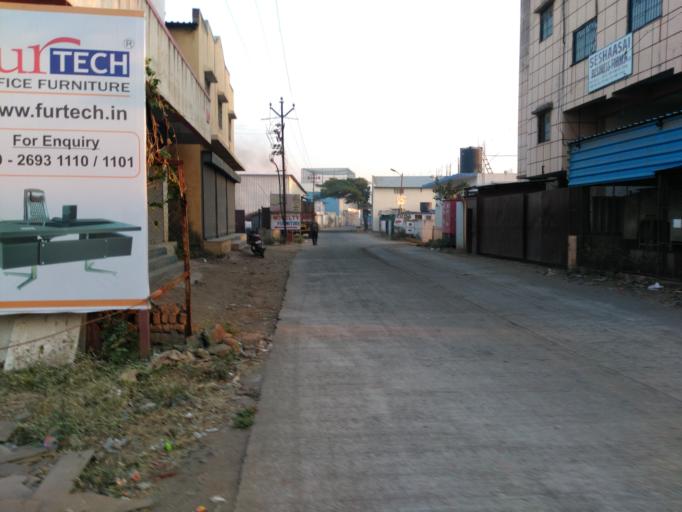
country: IN
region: Maharashtra
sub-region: Pune Division
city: Pune
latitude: 18.4518
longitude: 73.9022
